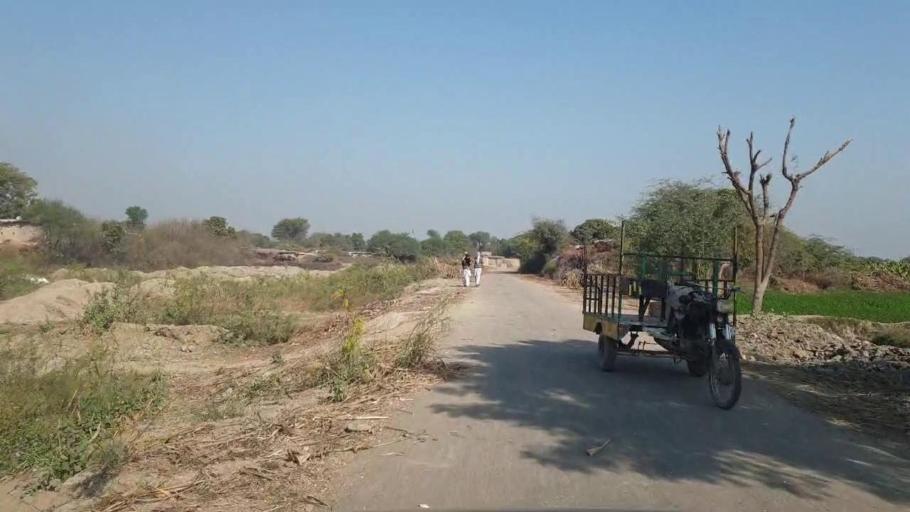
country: PK
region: Sindh
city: Tando Jam
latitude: 25.3774
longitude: 68.6379
